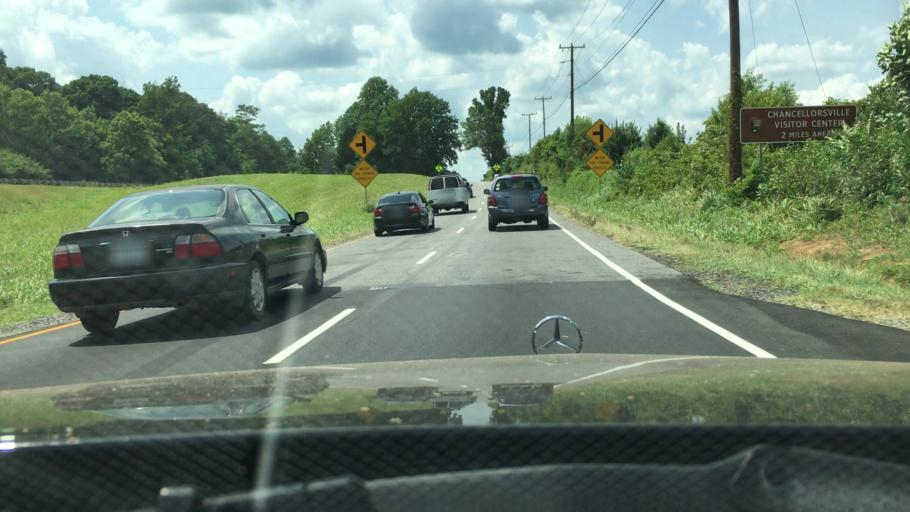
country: US
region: Virginia
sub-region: Spotsylvania County
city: Spotsylvania
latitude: 38.2996
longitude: -77.6104
